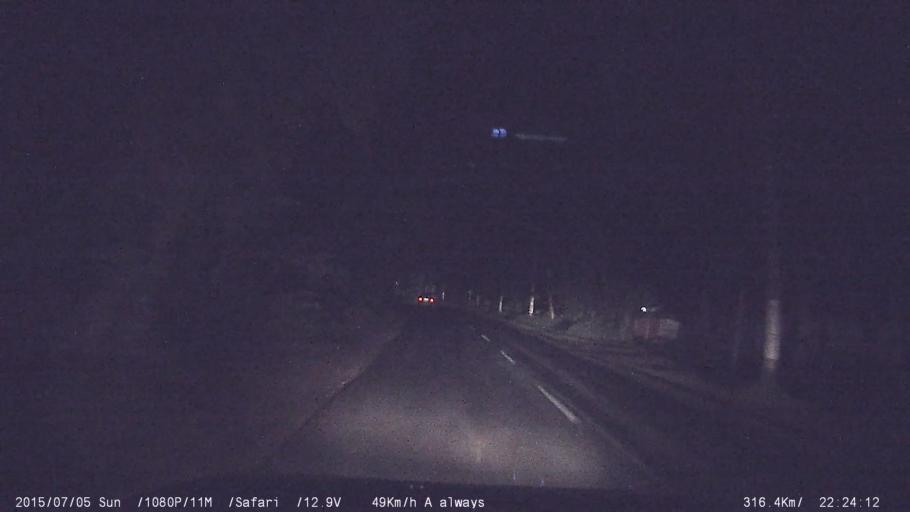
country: IN
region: Kerala
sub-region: Palakkad district
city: Palakkad
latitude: 10.8200
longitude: 76.5999
